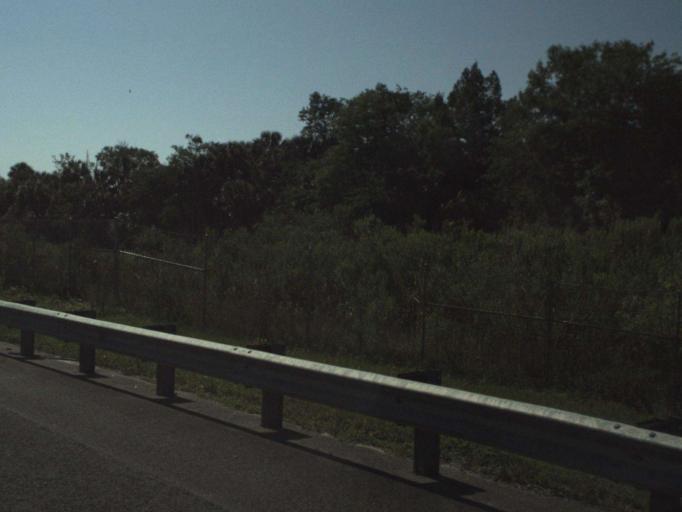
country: US
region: Florida
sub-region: Brevard County
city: Cocoa West
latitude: 28.3703
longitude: -80.8884
